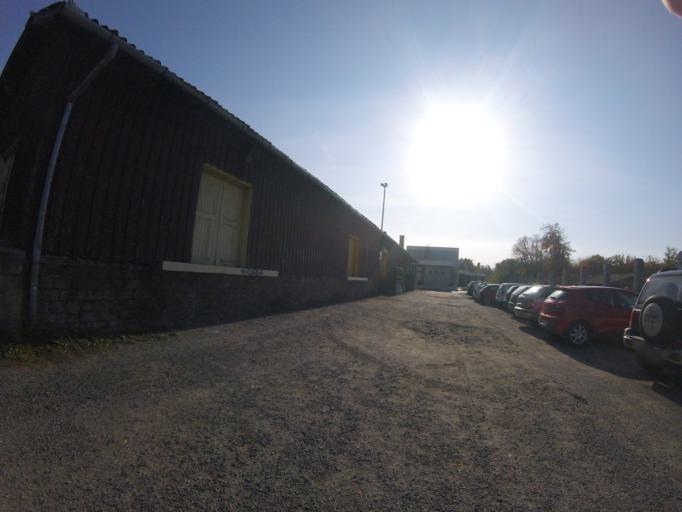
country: HU
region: Zala
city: Keszthely
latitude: 46.7585
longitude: 17.2479
